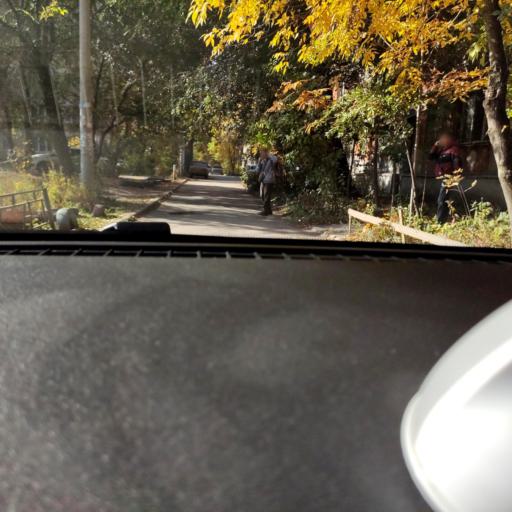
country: RU
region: Samara
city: Samara
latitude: 53.2132
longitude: 50.2554
